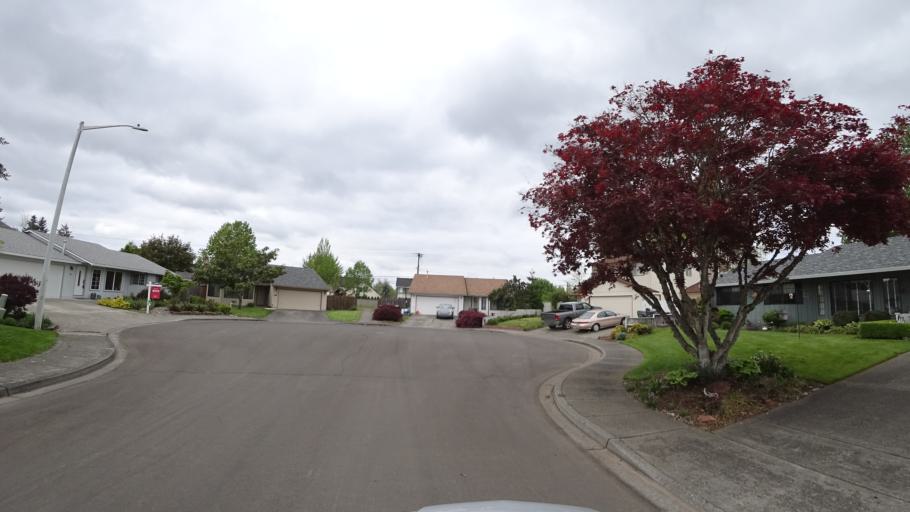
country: US
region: Oregon
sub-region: Washington County
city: Hillsboro
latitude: 45.5402
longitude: -122.9787
